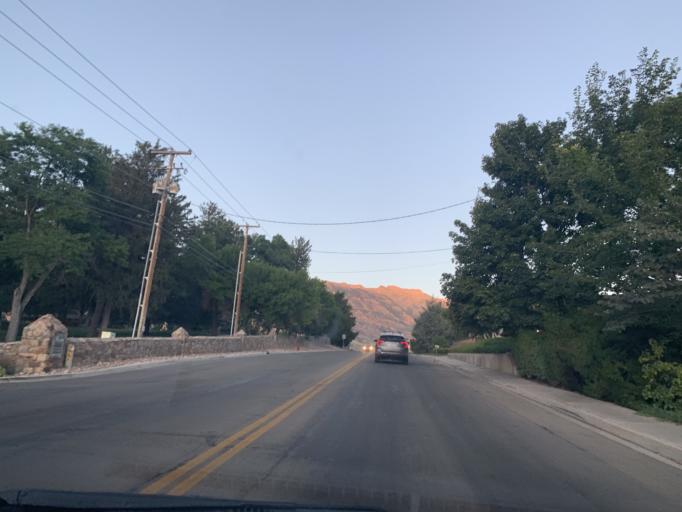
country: US
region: Utah
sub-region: Utah County
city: American Fork
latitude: 40.3918
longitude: -111.7753
